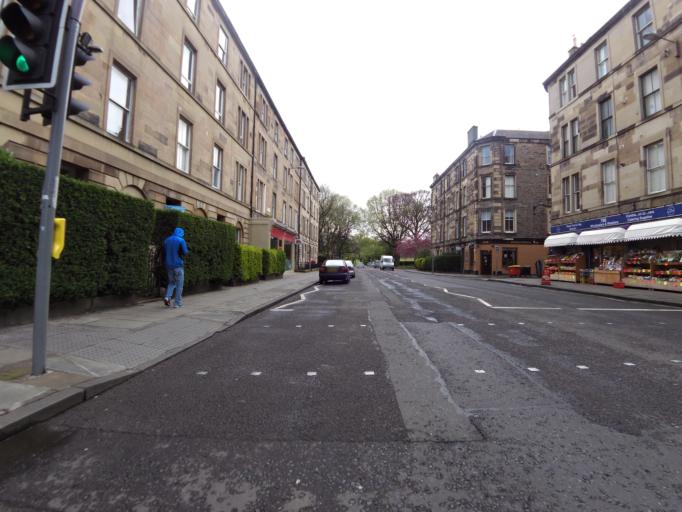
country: GB
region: Scotland
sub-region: Edinburgh
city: Edinburgh
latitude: 55.9427
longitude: -3.2014
